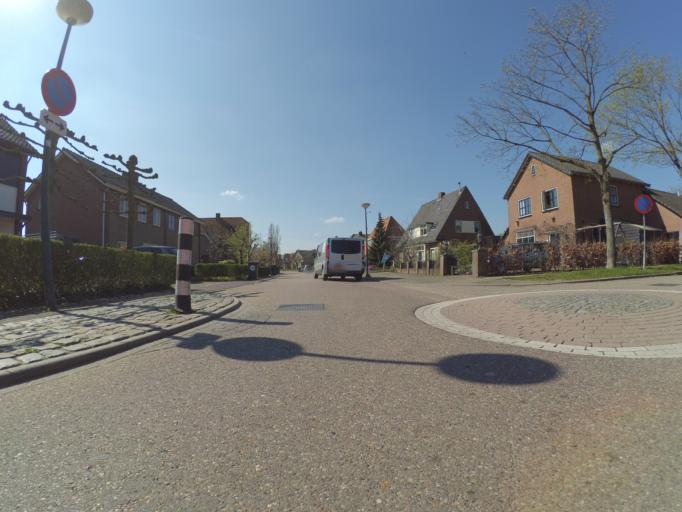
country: NL
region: Utrecht
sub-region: Gemeente Utrechtse Heuvelrug
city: Driebergen-Rijsenburg
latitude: 52.0224
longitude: 5.2446
